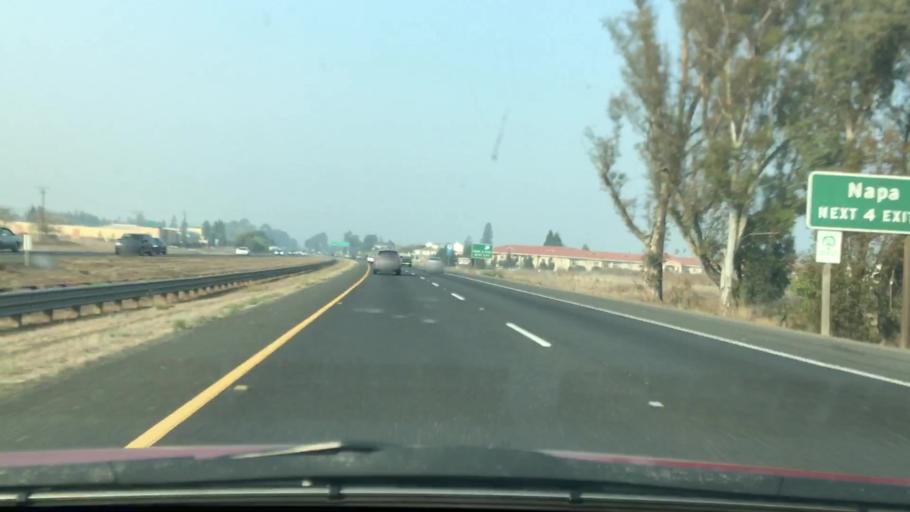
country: US
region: California
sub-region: Napa County
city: Napa
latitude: 38.2724
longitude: -122.2984
